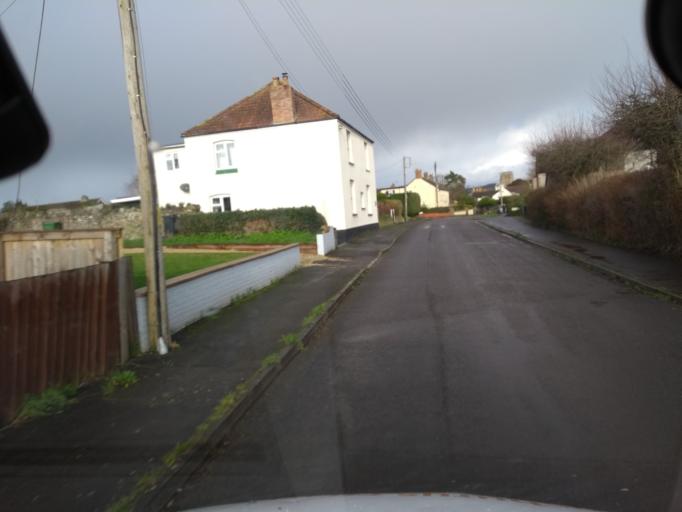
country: GB
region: England
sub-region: Somerset
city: Creech Saint Michael
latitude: 51.0180
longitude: -3.0504
